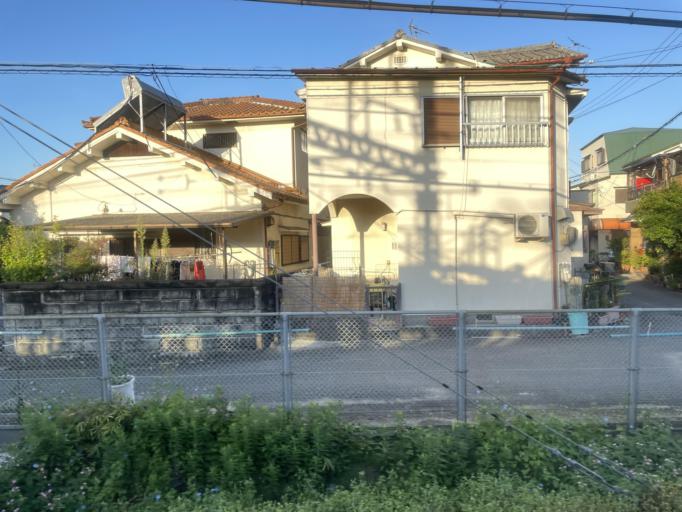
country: JP
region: Osaka
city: Matsubara
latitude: 34.5814
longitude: 135.5376
